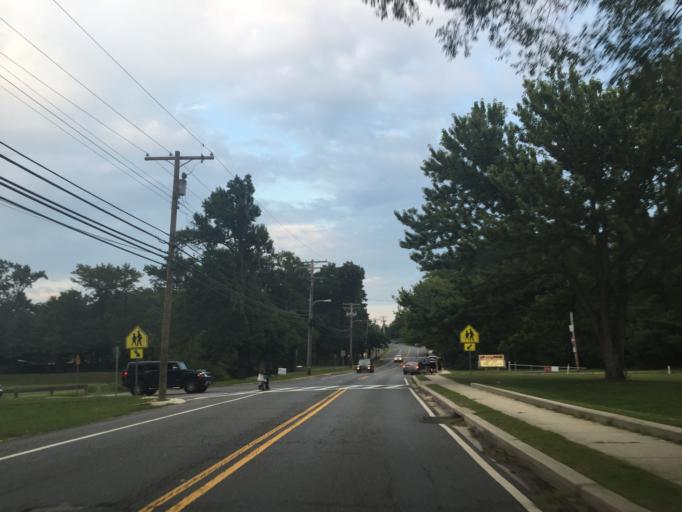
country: US
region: Maryland
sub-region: Anne Arundel County
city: Odenton
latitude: 39.0826
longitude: -76.6971
